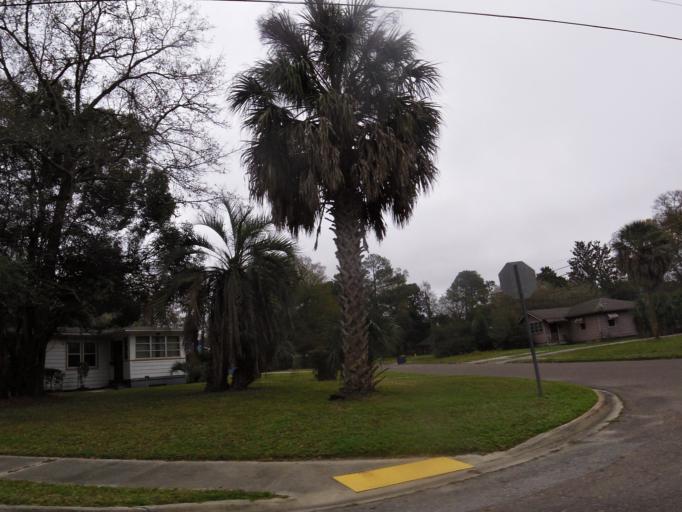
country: US
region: Florida
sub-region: Duval County
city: Jacksonville
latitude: 30.3674
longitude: -81.7019
